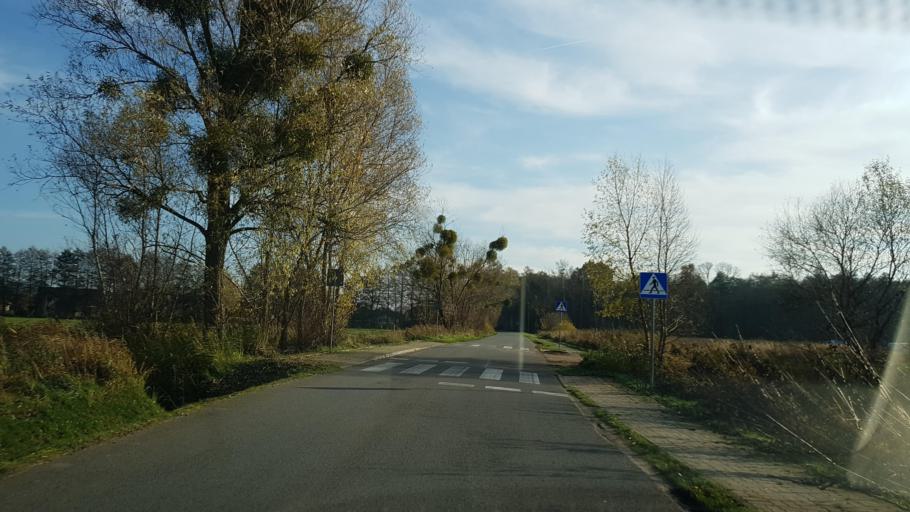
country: PL
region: West Pomeranian Voivodeship
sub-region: Powiat policki
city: Dobra
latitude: 53.4947
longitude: 14.3688
